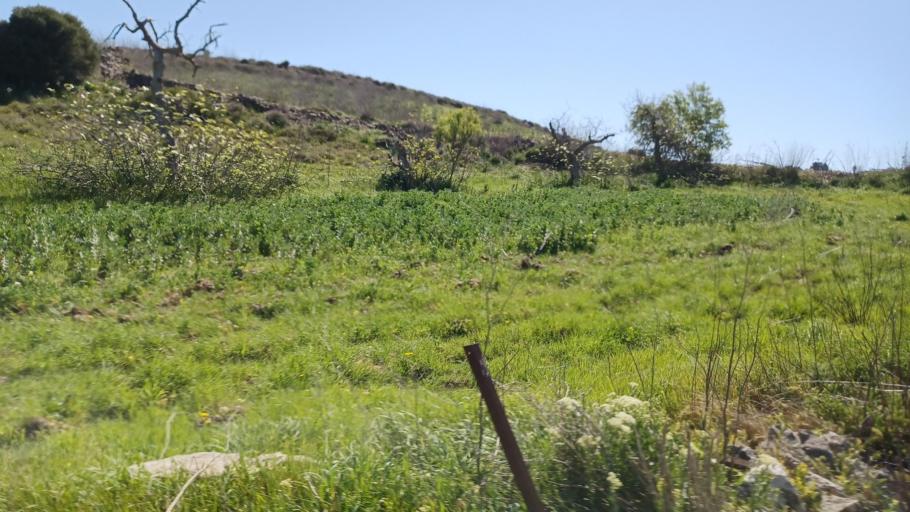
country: CY
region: Pafos
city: Polis
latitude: 34.9666
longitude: 32.3880
